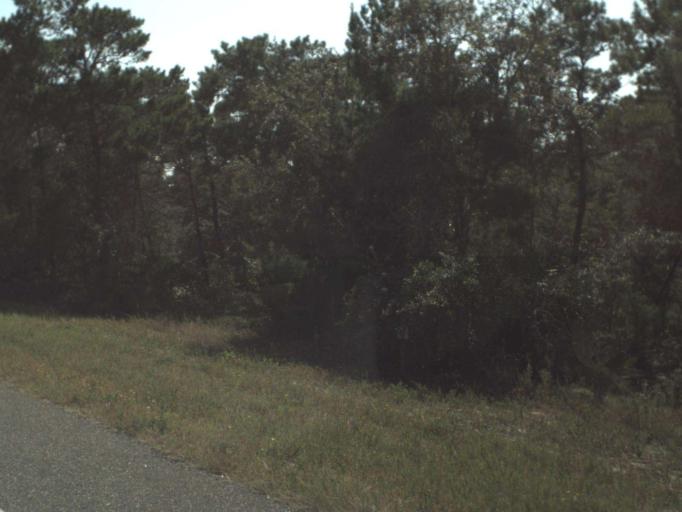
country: US
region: Florida
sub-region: Gulf County
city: Port Saint Joe
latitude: 29.7080
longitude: -85.3799
